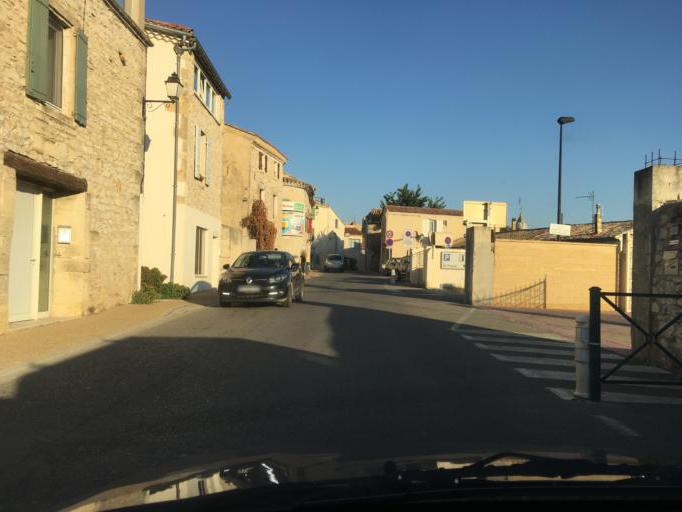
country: FR
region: Languedoc-Roussillon
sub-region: Departement du Gard
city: Tavel
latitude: 44.0121
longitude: 4.6994
